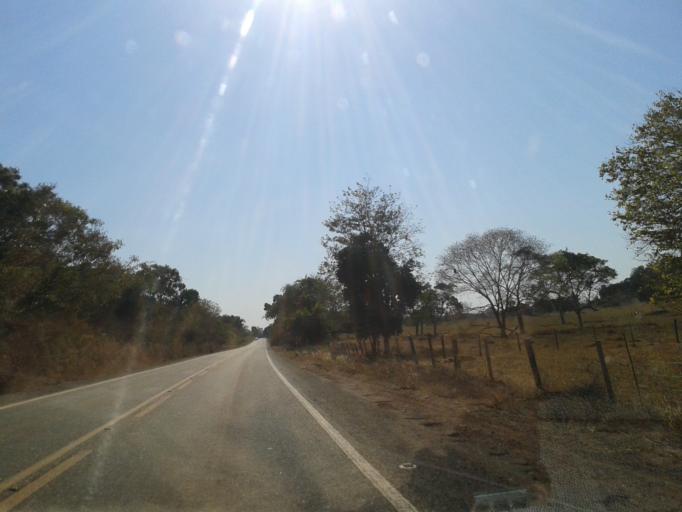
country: BR
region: Goias
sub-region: Mozarlandia
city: Mozarlandia
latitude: -14.6584
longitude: -50.5281
